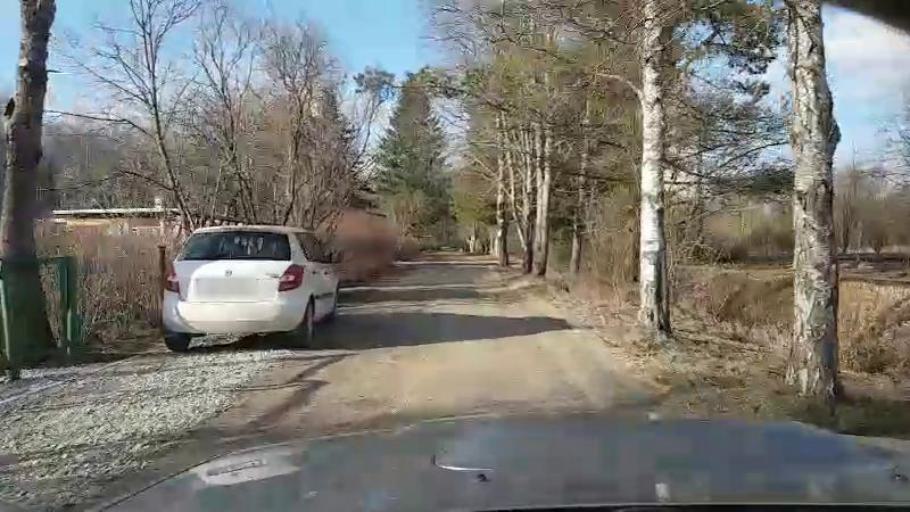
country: EE
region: Jaervamaa
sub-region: Paide linn
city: Paide
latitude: 58.8890
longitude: 25.5313
